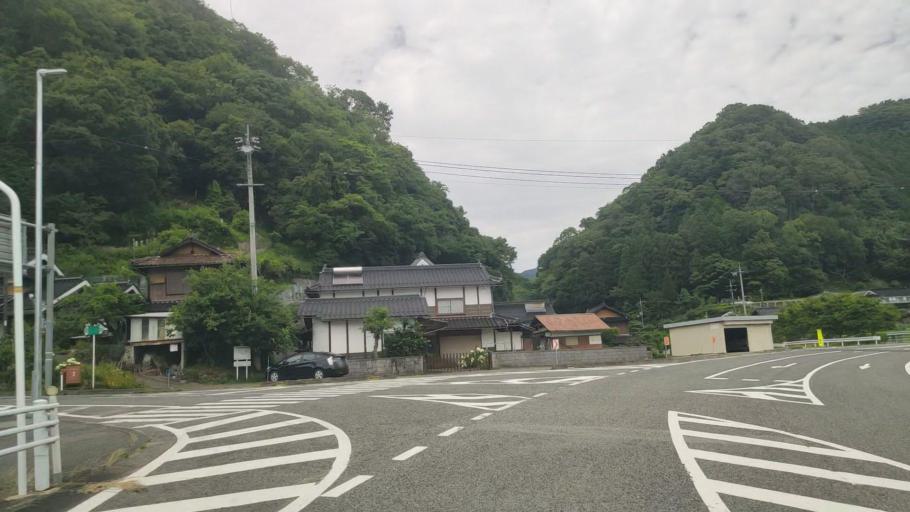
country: JP
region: Hyogo
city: Yamazakicho-nakabirose
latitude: 35.1057
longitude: 134.2978
